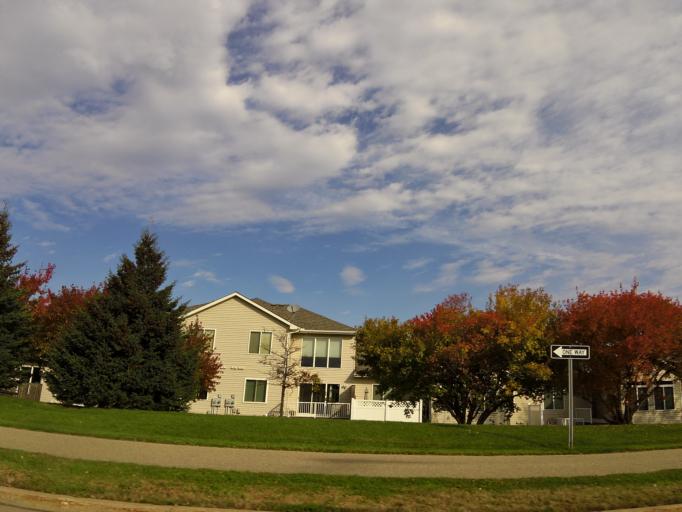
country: US
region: Minnesota
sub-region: Dakota County
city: Eagan
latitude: 44.8050
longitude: -93.2245
